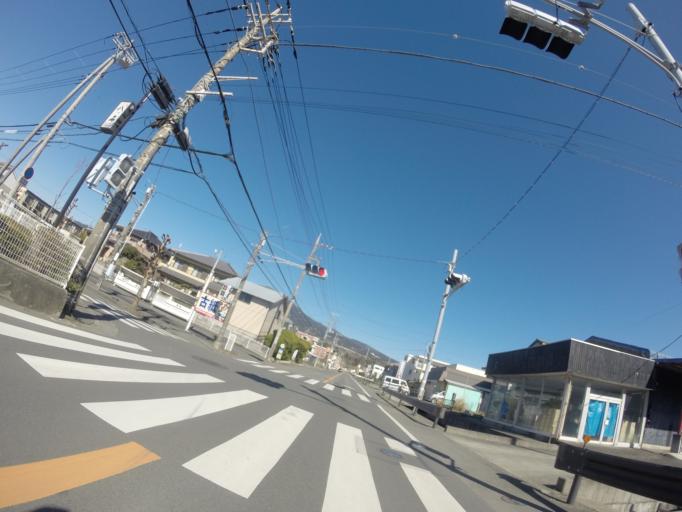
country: JP
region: Shizuoka
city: Numazu
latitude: 35.1350
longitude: 138.8039
